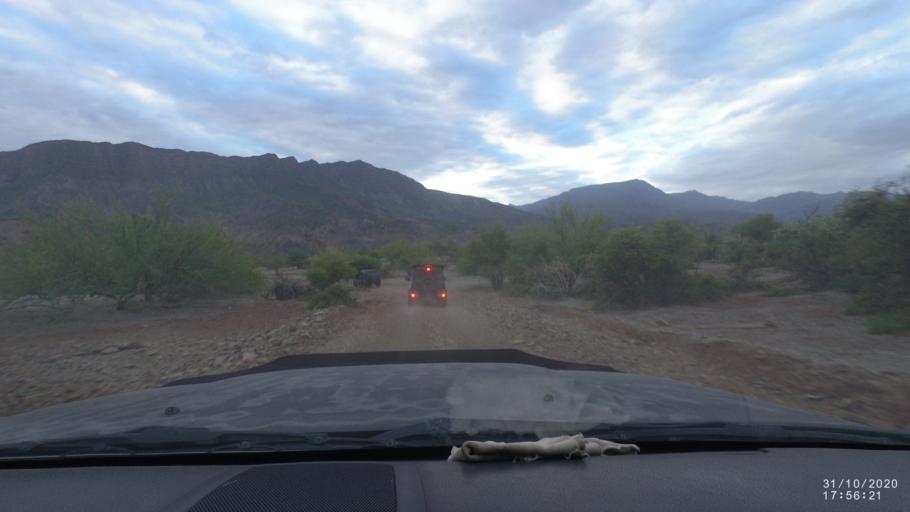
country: BO
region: Chuquisaca
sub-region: Provincia Zudanez
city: Mojocoya
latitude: -18.6485
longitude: -64.5296
